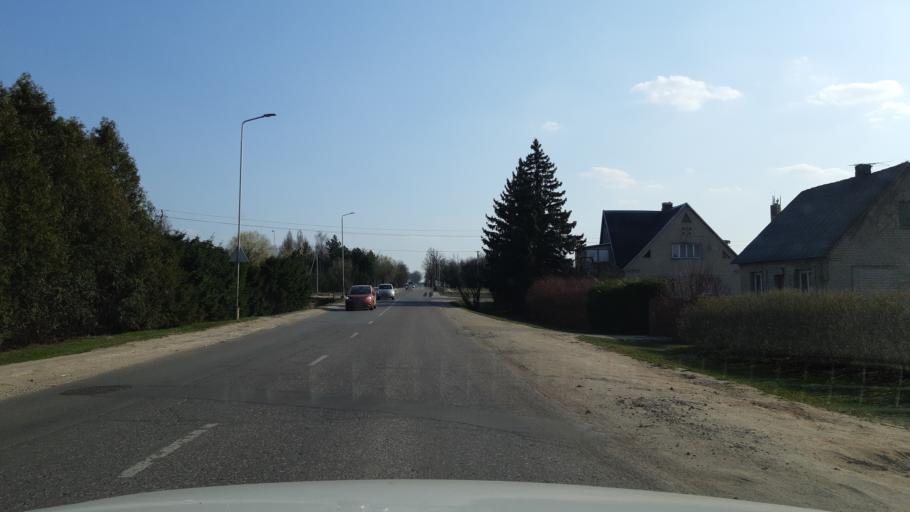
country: LT
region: Kauno apskritis
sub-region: Kaunas
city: Aleksotas
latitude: 54.8338
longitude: 23.9467
